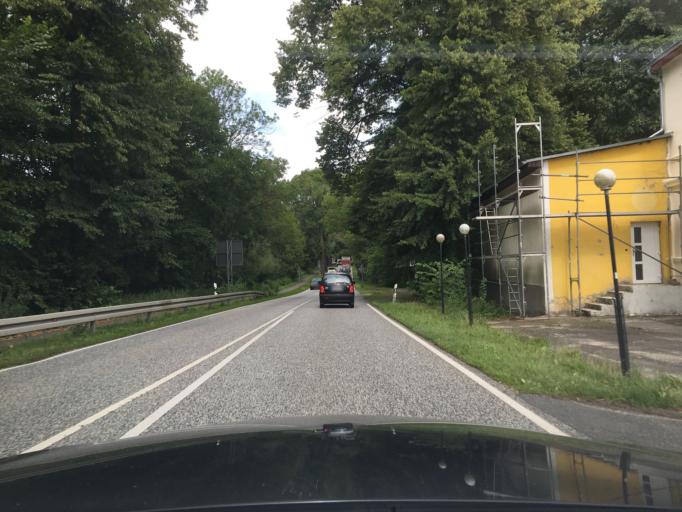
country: DE
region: Brandenburg
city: Gransee
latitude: 53.0726
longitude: 13.1814
